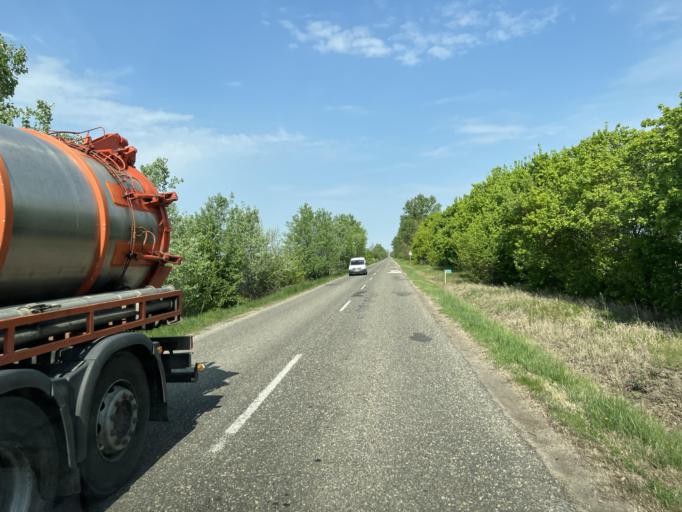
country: HU
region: Pest
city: Tortel
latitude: 47.1083
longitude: 19.9849
